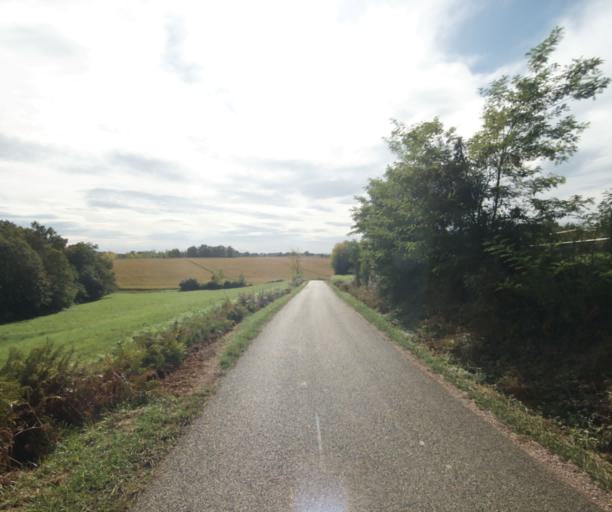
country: FR
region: Midi-Pyrenees
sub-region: Departement du Gers
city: Cazaubon
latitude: 43.9009
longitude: -0.1588
